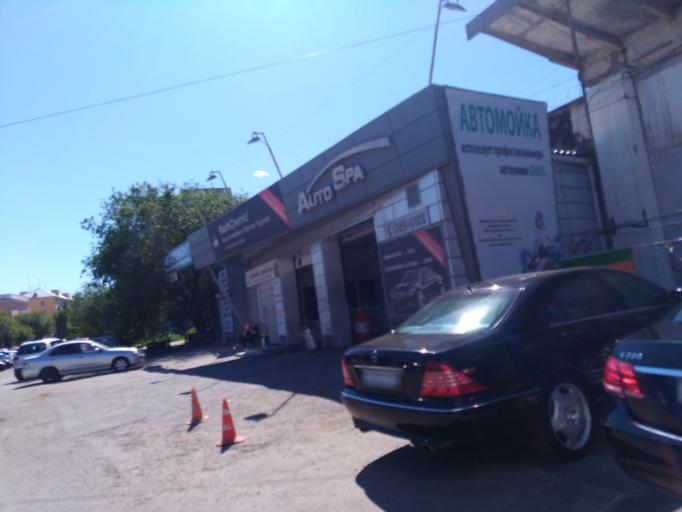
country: RU
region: Volgograd
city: Volgograd
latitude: 48.7169
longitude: 44.5252
